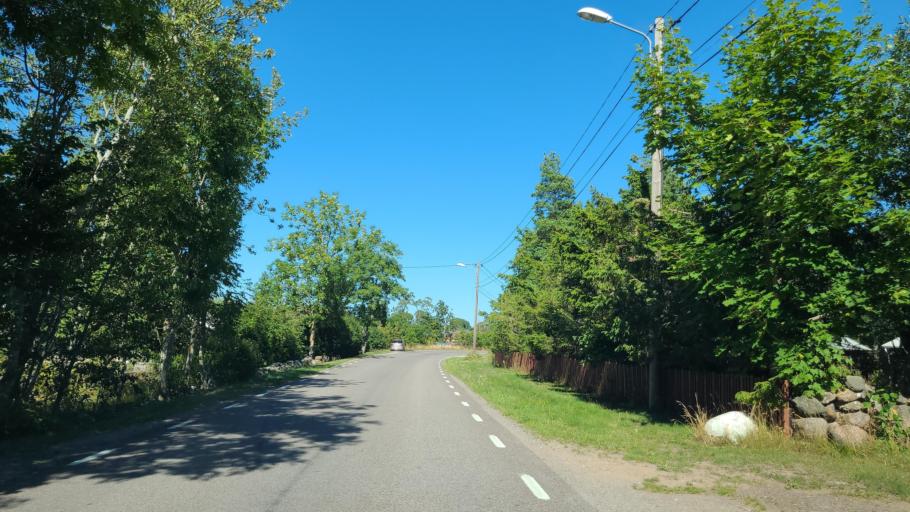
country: SE
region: Kalmar
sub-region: Borgholms Kommun
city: Borgholm
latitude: 56.8408
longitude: 16.7877
